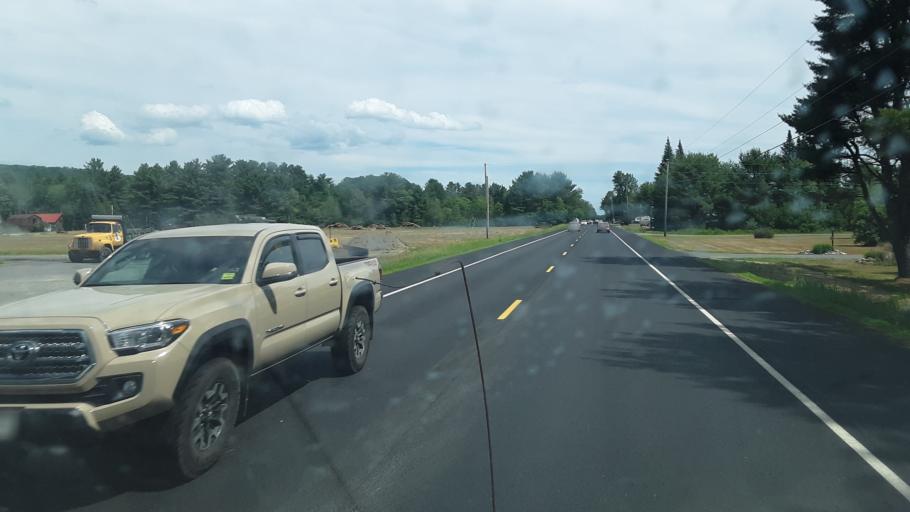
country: US
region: Maine
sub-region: Somerset County
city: Norridgewock
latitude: 44.7031
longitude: -69.7659
